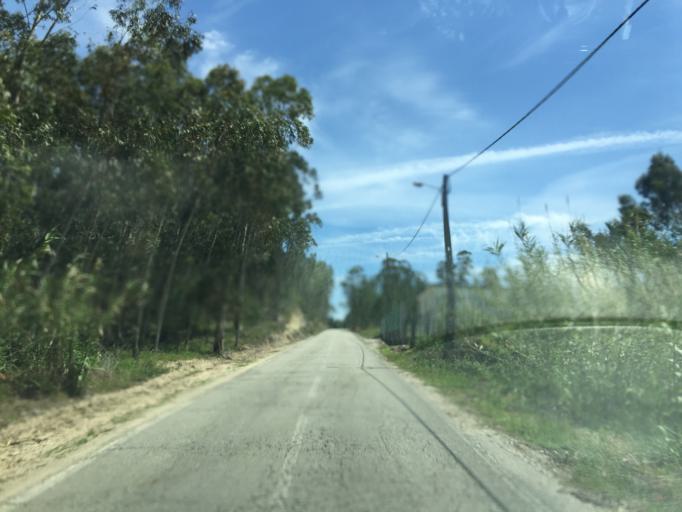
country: PT
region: Leiria
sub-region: Pombal
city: Lourical
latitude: 40.0661
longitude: -8.7240
